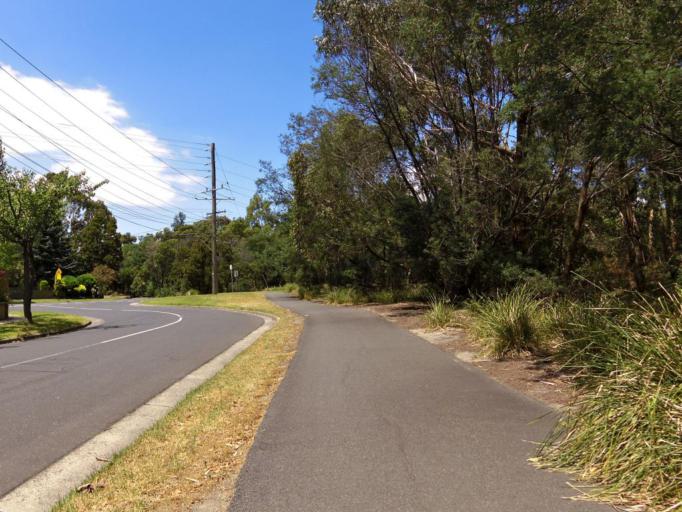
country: AU
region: Victoria
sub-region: Monash
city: Chadstone
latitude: -37.8883
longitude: 145.0911
